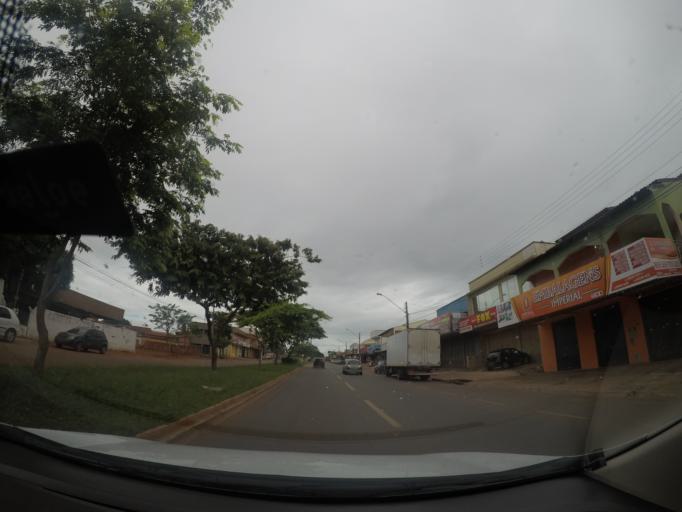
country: BR
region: Goias
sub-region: Goiania
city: Goiania
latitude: -16.6259
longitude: -49.3339
